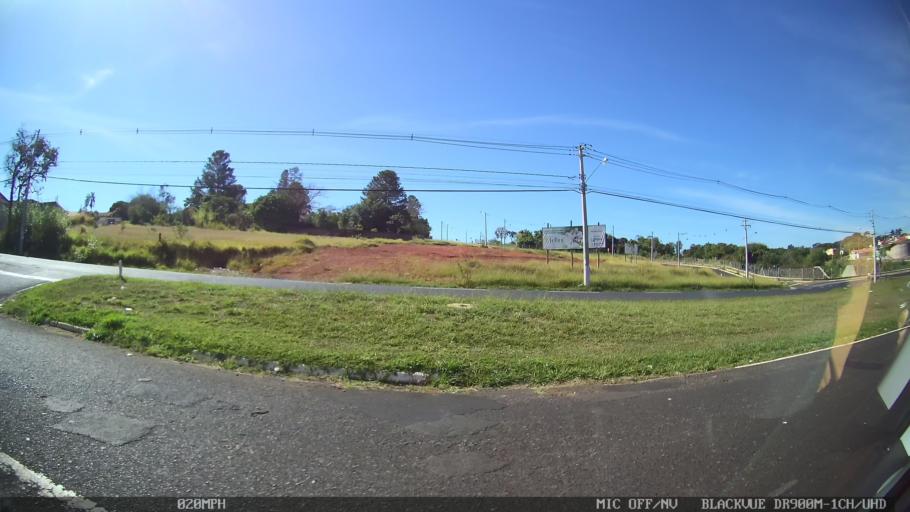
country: BR
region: Sao Paulo
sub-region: Franca
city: Franca
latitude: -20.5542
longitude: -47.3714
